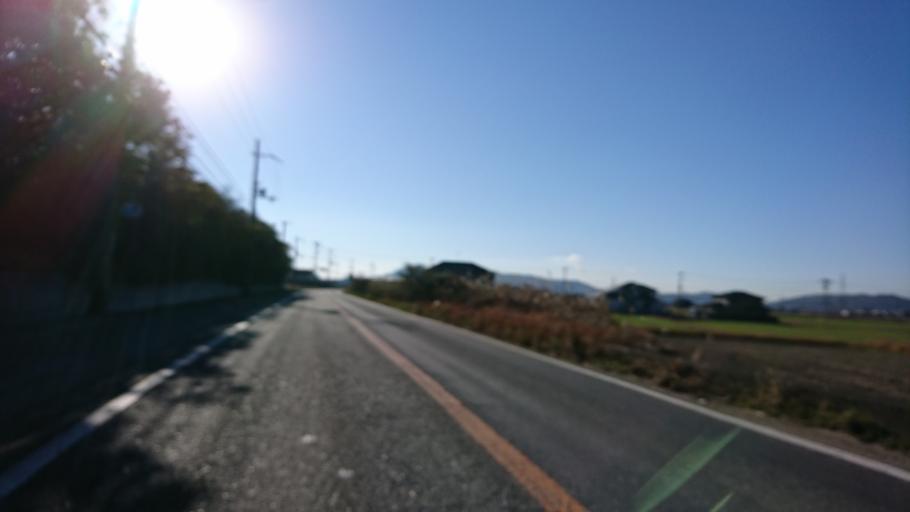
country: JP
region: Hyogo
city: Kakogawacho-honmachi
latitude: 34.8409
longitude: 134.8381
